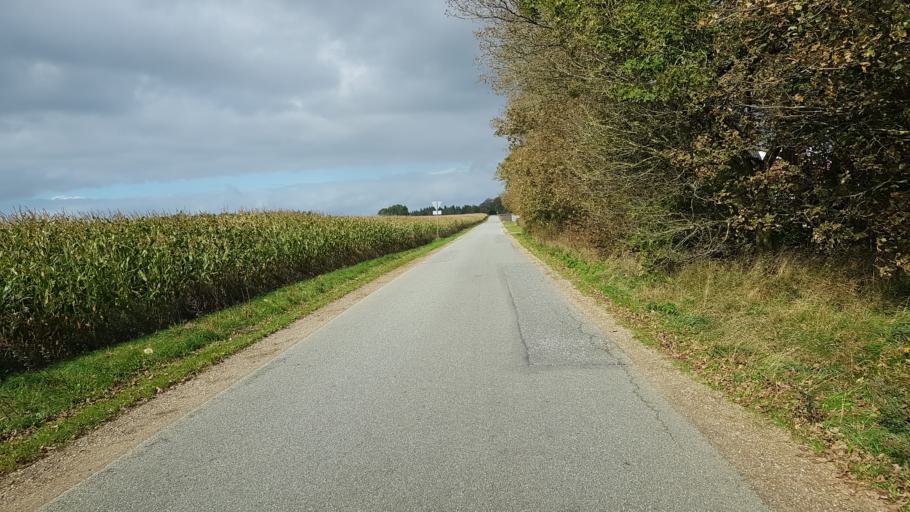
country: DK
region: South Denmark
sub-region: Billund Kommune
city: Grindsted
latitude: 55.6592
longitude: 8.7920
